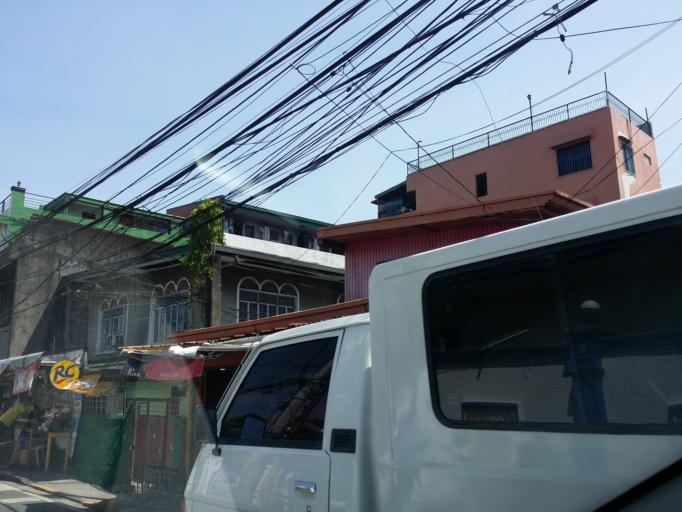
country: PH
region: Metro Manila
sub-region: Mandaluyong
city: Mandaluyong City
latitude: 14.5781
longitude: 121.0268
